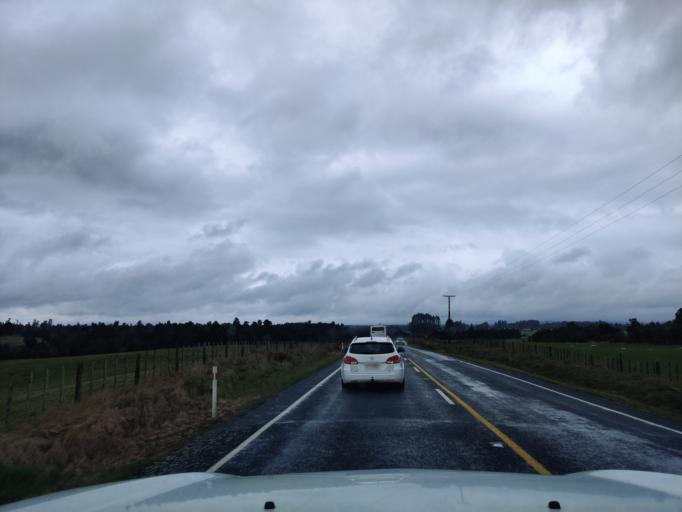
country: NZ
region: Manawatu-Wanganui
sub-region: Ruapehu District
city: Waiouru
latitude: -39.3534
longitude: 175.3575
